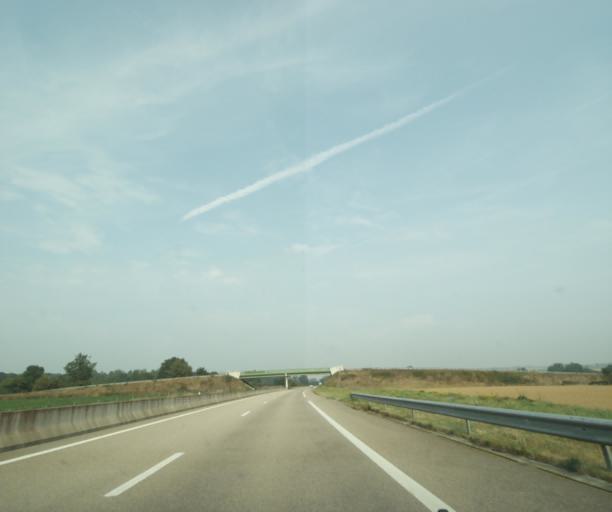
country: FR
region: Lower Normandy
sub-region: Departement de l'Orne
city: Ecouche
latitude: 48.7804
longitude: -0.1200
